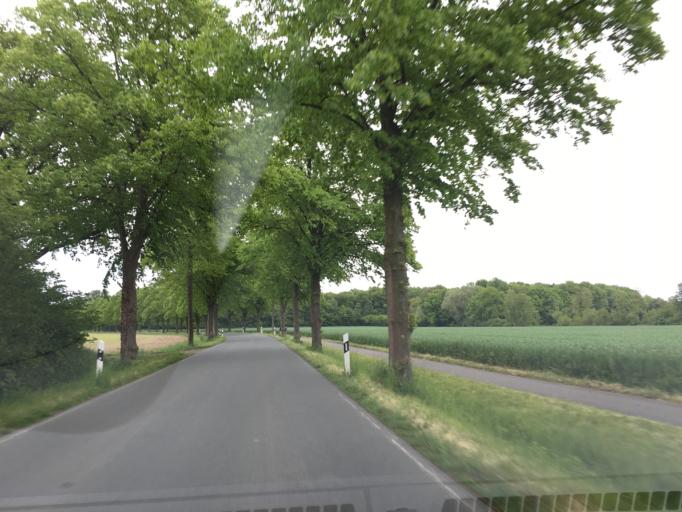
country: DE
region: North Rhine-Westphalia
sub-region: Regierungsbezirk Munster
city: Senden
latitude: 51.9303
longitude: 7.5019
